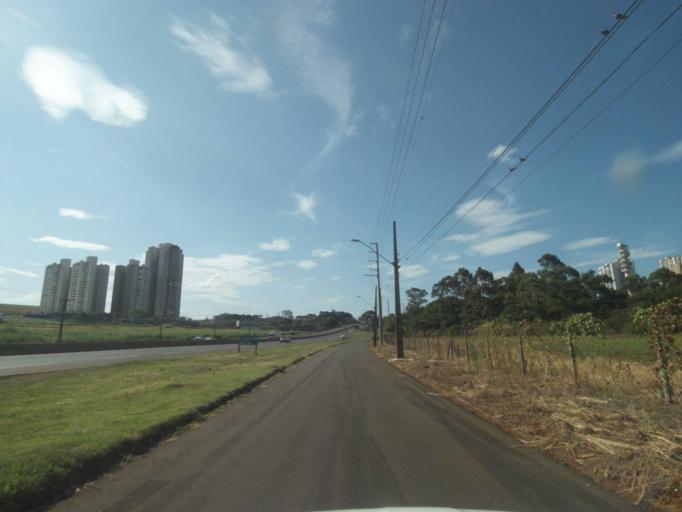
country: BR
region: Parana
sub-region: Londrina
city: Londrina
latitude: -23.3400
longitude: -51.1825
